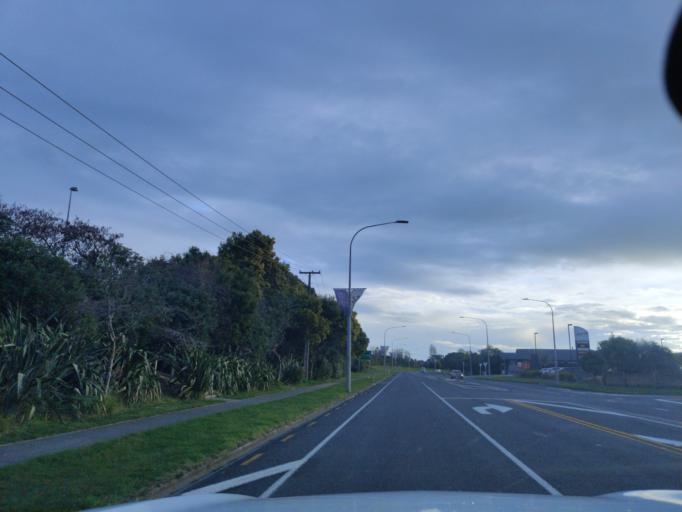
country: NZ
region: Manawatu-Wanganui
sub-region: Palmerston North City
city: Palmerston North
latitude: -40.3875
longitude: 175.6403
